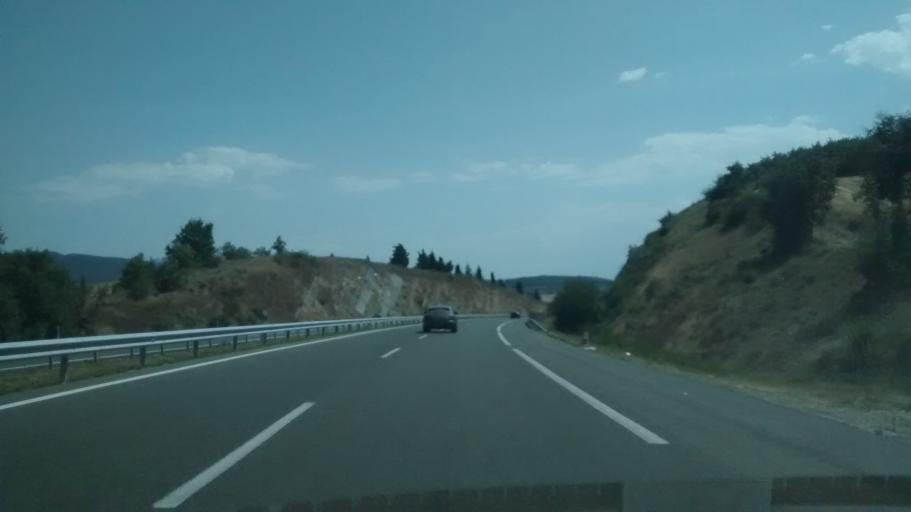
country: ES
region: Basque Country
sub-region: Provincia de Alava
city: Arminon
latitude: 42.6964
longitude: -2.8934
